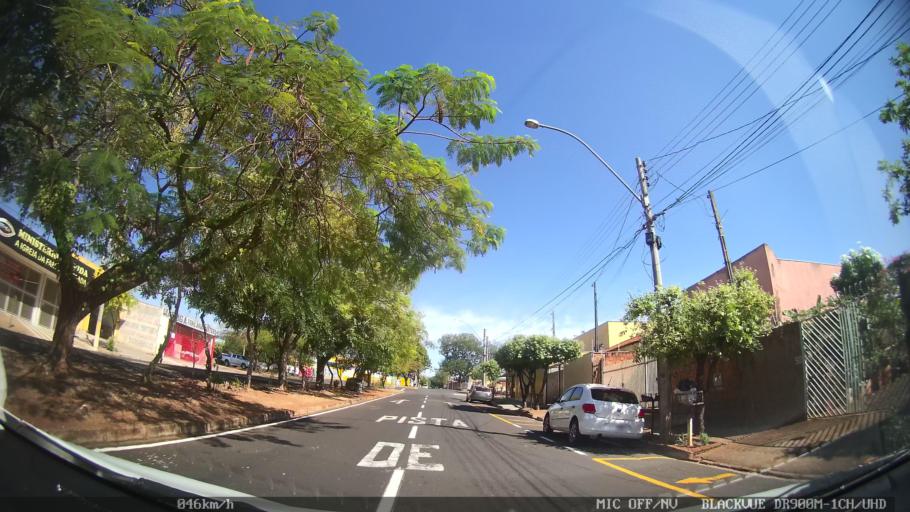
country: BR
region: Sao Paulo
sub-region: Sao Jose Do Rio Preto
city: Sao Jose do Rio Preto
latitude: -20.7669
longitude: -49.4074
